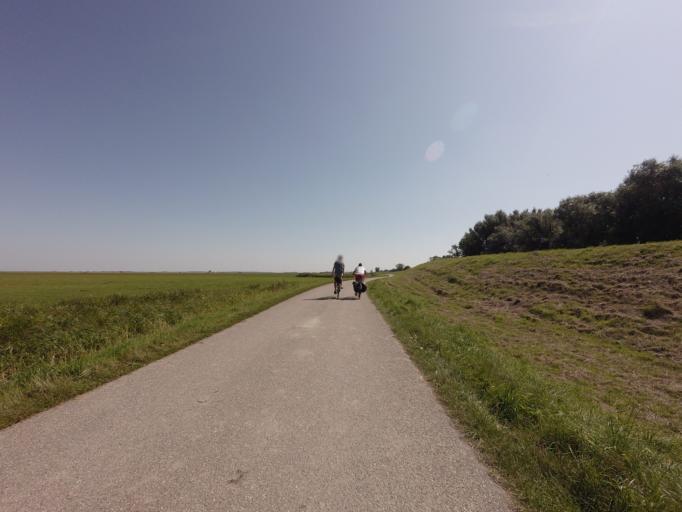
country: NL
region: Friesland
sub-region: Gemeente Dongeradeel
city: Anjum
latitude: 53.3945
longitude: 6.1114
